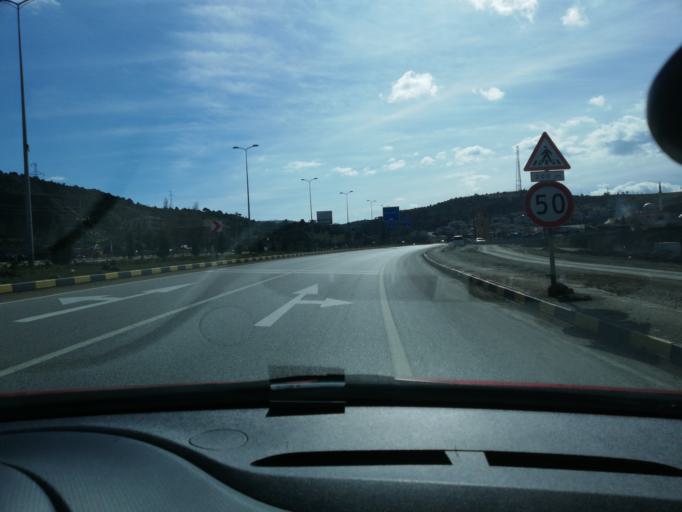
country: TR
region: Karabuk
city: Eskipazar
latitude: 40.9625
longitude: 32.5562
